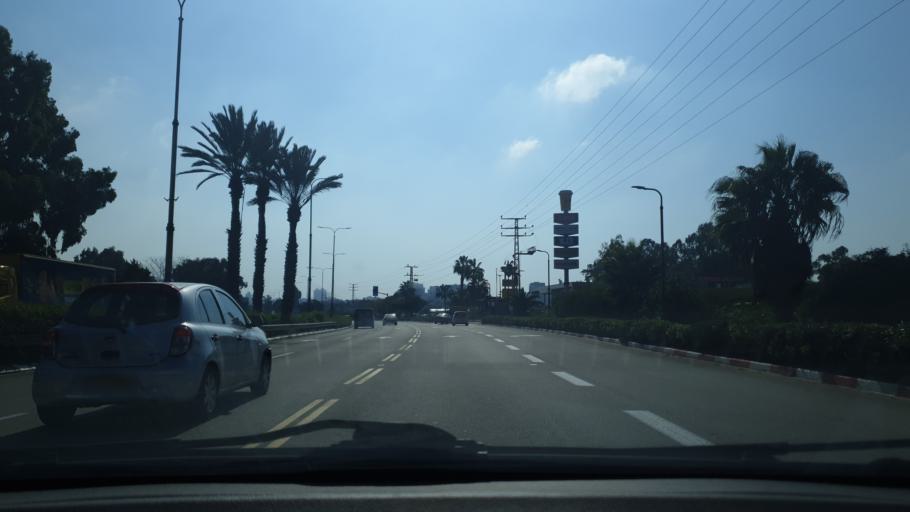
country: IL
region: Central District
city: Bet Dagan
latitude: 31.9922
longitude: 34.8131
